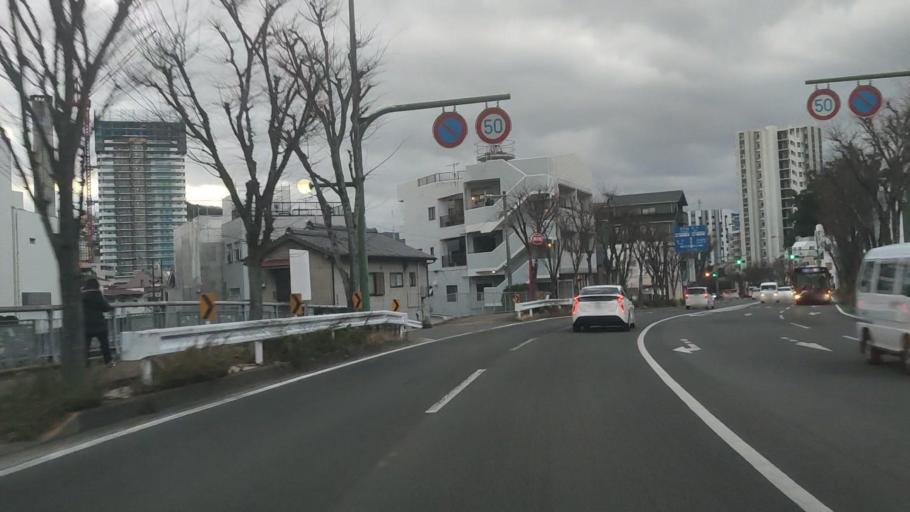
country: JP
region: Nagasaki
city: Nagasaki-shi
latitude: 32.7566
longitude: 129.8864
